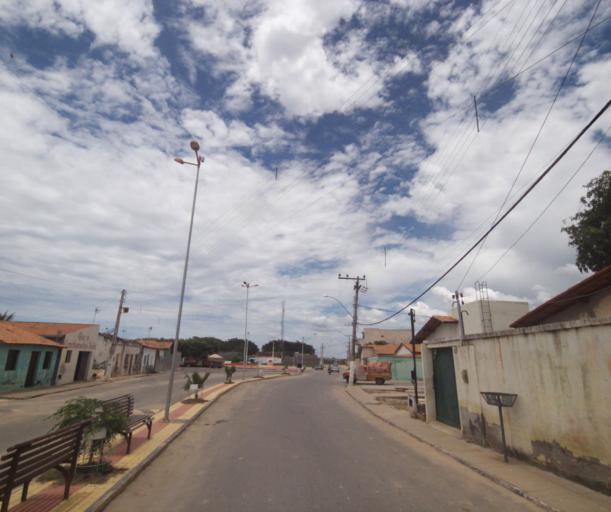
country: BR
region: Bahia
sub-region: Carinhanha
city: Carinhanha
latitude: -14.3345
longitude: -43.7718
